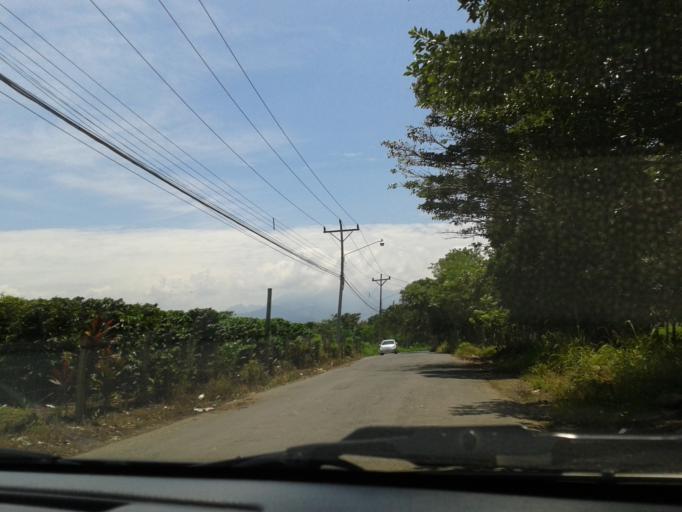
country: CR
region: Alajuela
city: Alajuela
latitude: 9.9981
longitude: -84.2345
